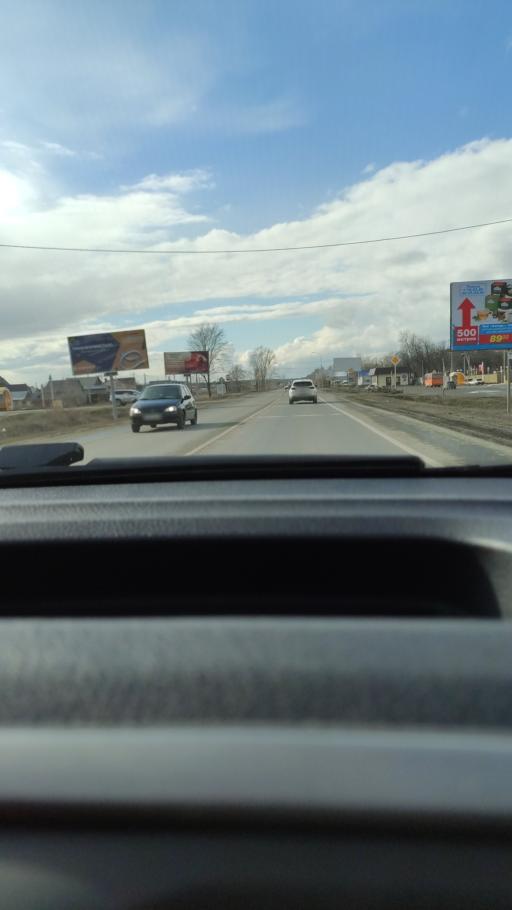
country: RU
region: Samara
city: Kurumoch
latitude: 53.4839
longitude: 50.0309
